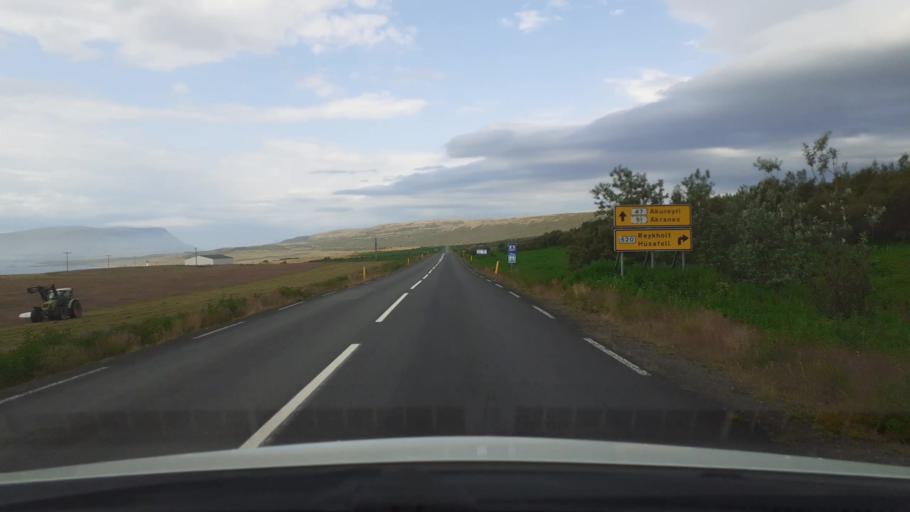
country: IS
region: Capital Region
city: Mosfellsbaer
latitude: 64.4102
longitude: -21.6012
